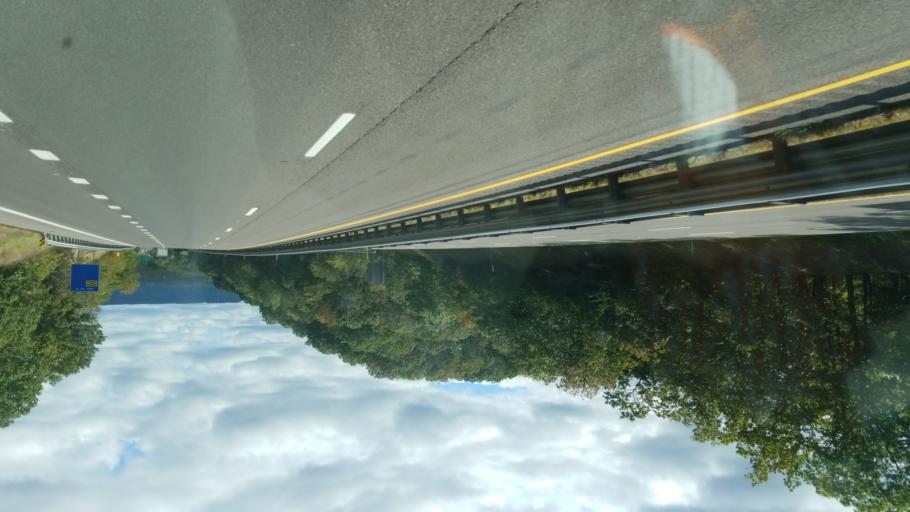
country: US
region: Maryland
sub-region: Washington County
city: Hancock
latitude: 39.7035
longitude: -78.1690
